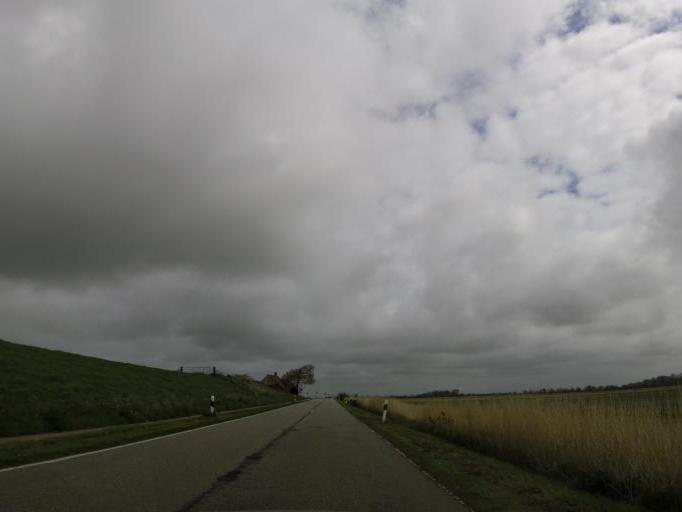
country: DE
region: Schleswig-Holstein
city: Dagebull
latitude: 54.7399
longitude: 8.7232
